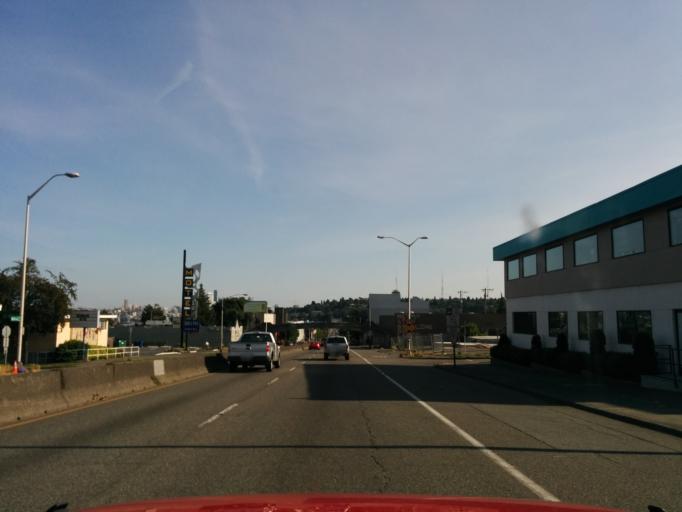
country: US
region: Washington
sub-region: King County
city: Seattle
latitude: 47.6582
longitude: -122.3475
